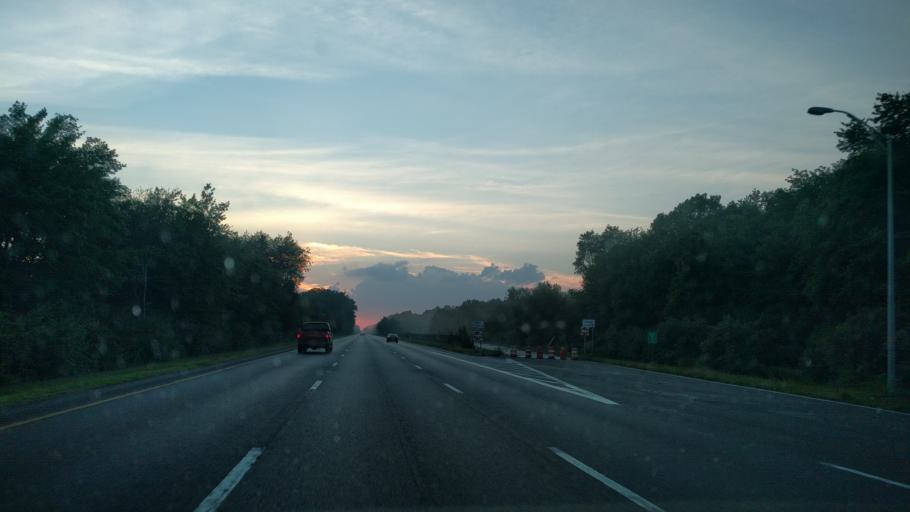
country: US
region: Massachusetts
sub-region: Bristol County
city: Seekonk
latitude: 41.7862
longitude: -71.2965
